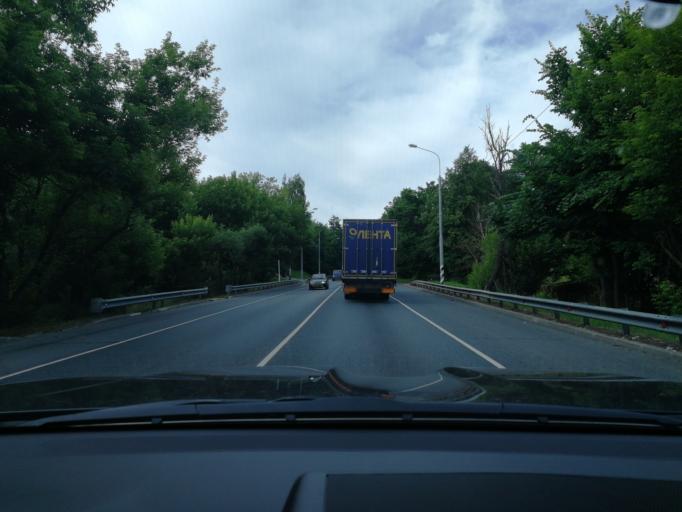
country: RU
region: Moskovskaya
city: Popovo
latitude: 55.0582
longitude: 37.7648
